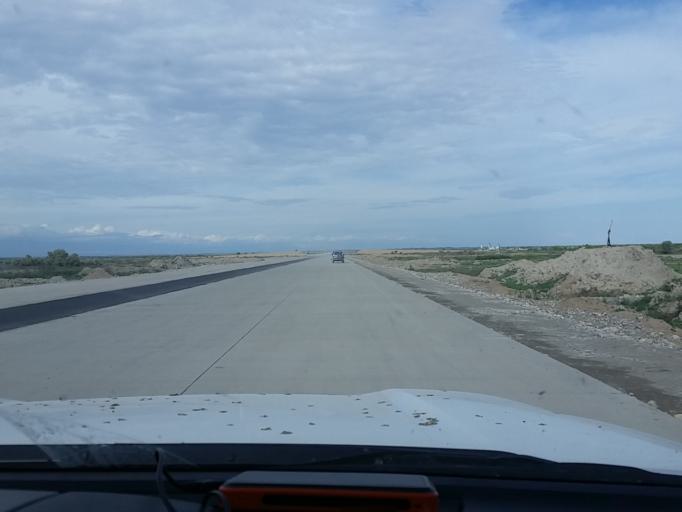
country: KZ
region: Almaty Oblysy
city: Zharkent
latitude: 44.0399
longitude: 79.9666
